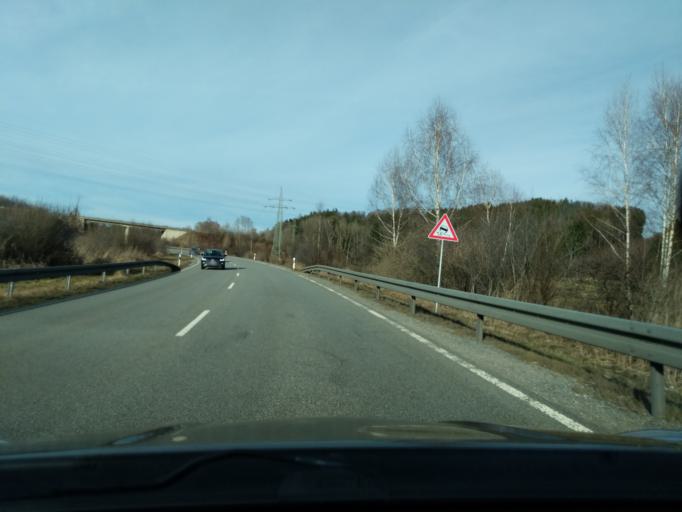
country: DE
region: Bavaria
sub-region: Upper Bavaria
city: Ebersberg
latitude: 48.0645
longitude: 11.9772
